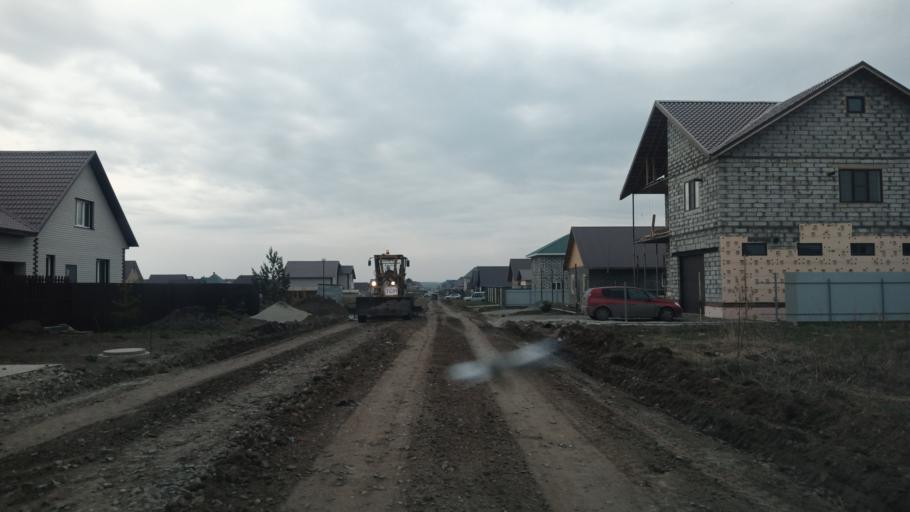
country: RU
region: Altai Krai
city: Yuzhnyy
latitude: 53.2275
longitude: 83.6912
